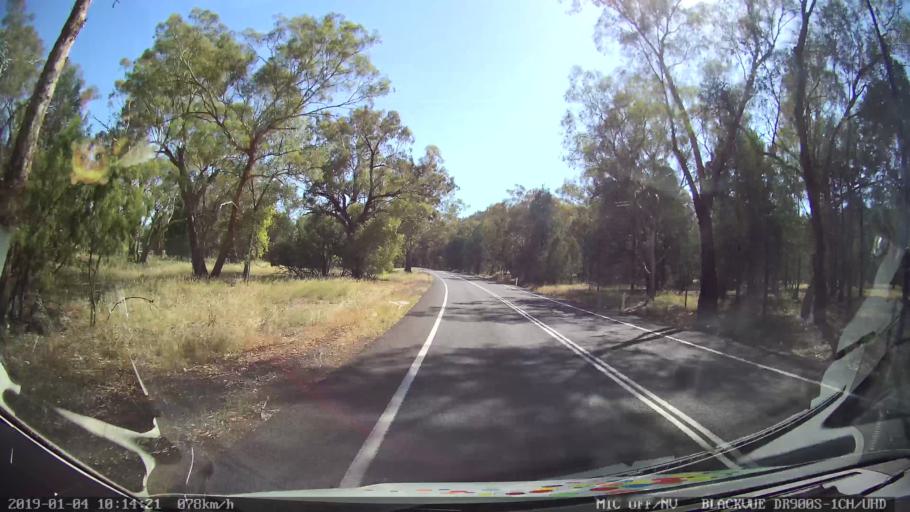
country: AU
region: New South Wales
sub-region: Cabonne
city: Canowindra
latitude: -33.3976
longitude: 148.4126
